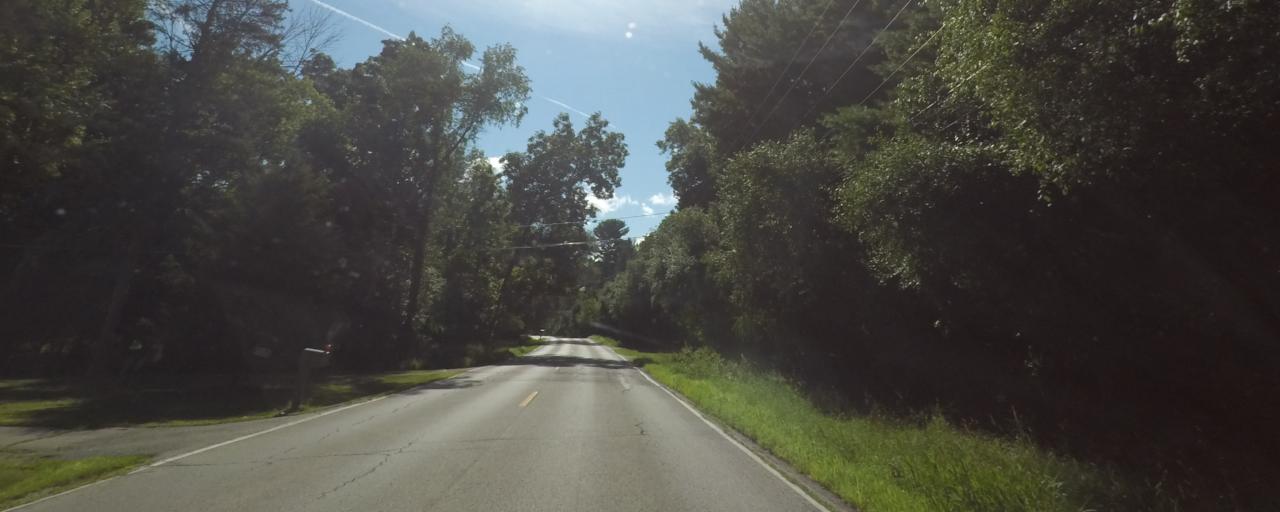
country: US
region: Wisconsin
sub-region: Waukesha County
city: Oconomowoc
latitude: 43.0828
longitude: -88.5012
